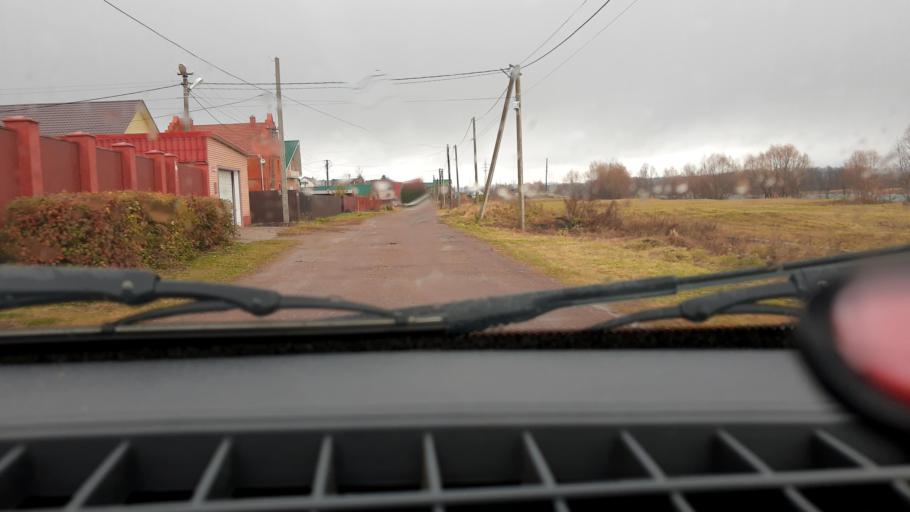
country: RU
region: Bashkortostan
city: Ufa
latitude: 54.8201
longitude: 55.9914
